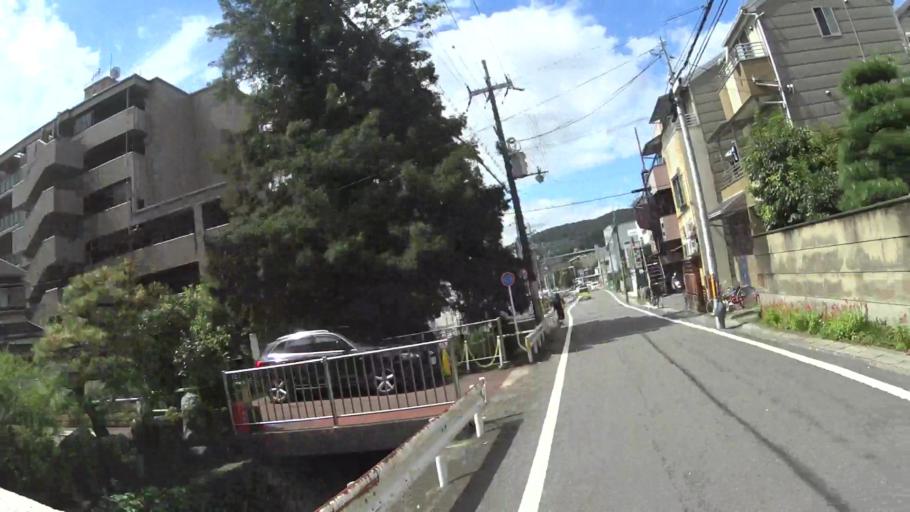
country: JP
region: Shiga Prefecture
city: Otsu-shi
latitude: 34.9611
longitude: 135.8143
